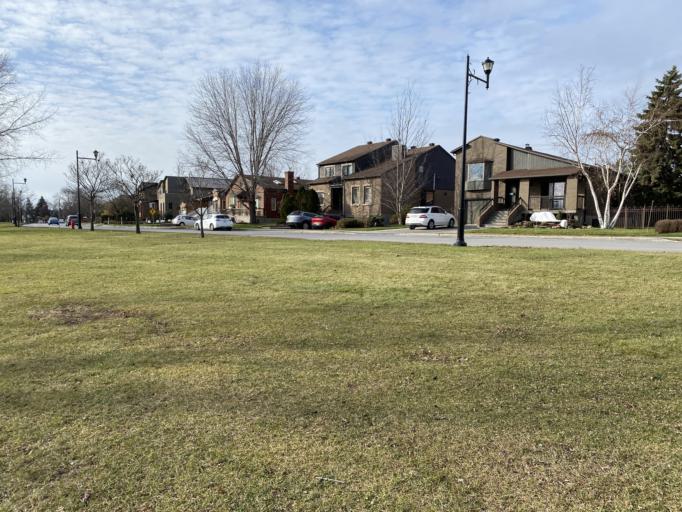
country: CA
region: Quebec
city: Saint-Raymond
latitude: 45.4252
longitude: -73.5968
